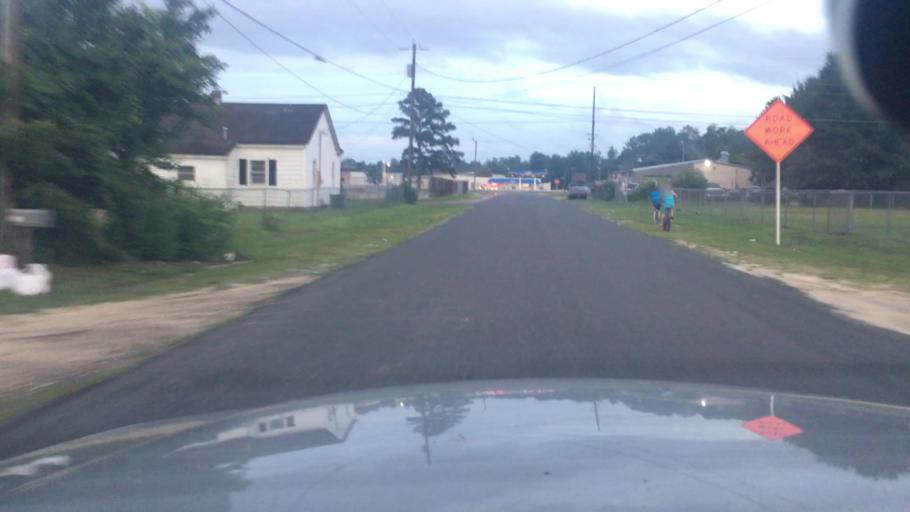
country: US
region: North Carolina
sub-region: Cumberland County
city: Hope Mills
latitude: 34.9831
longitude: -78.9085
